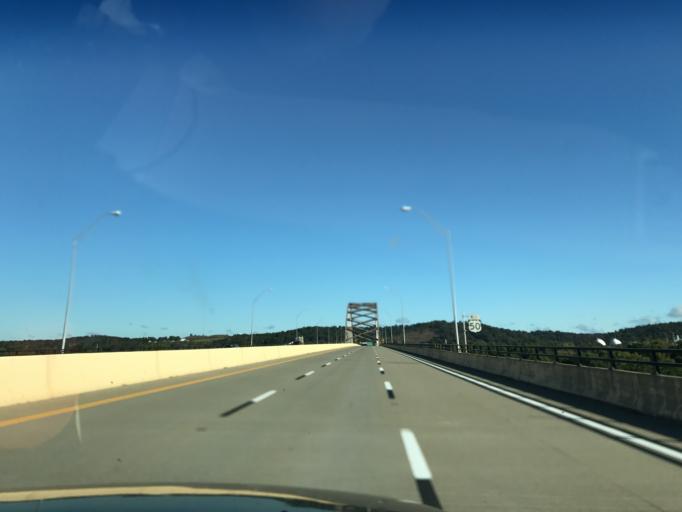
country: US
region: West Virginia
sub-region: Wood County
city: Blennerhassett
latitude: 39.2704
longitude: -81.6465
